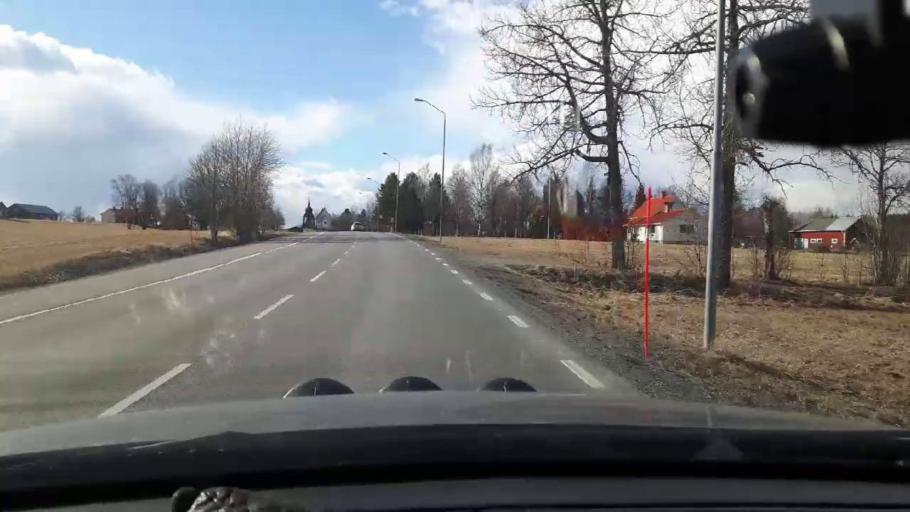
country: SE
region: Jaemtland
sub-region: OEstersunds Kommun
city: Ostersund
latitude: 63.1760
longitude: 14.5300
